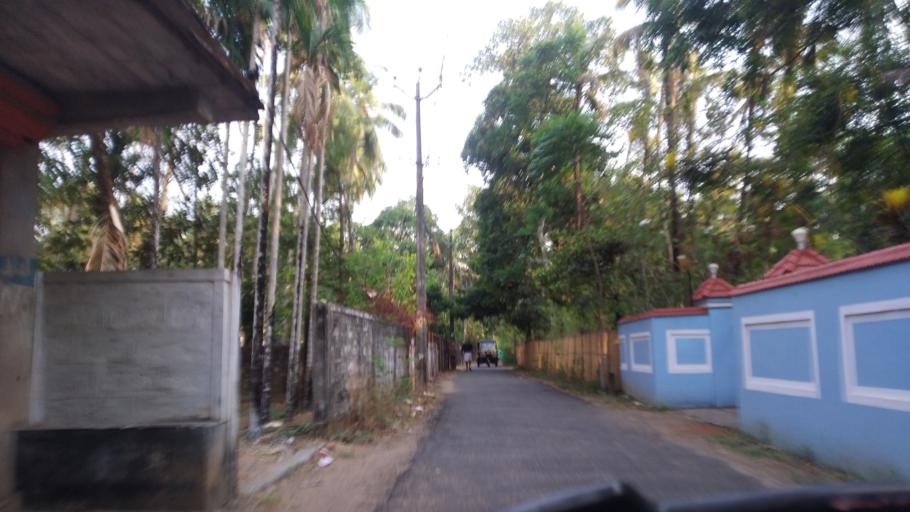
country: IN
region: Kerala
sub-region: Thrissur District
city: Thanniyam
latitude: 10.4138
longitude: 76.0877
